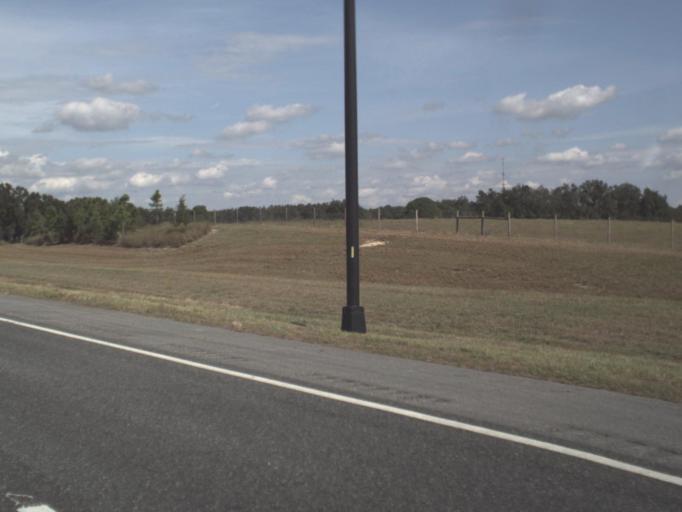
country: US
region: Florida
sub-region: Polk County
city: Polk City
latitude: 28.1408
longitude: -81.8417
